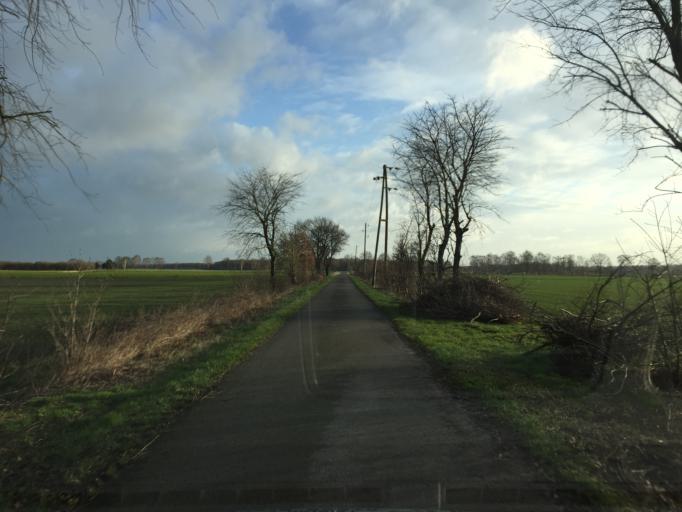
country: DE
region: Lower Saxony
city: Borstel
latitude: 52.6161
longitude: 8.9433
